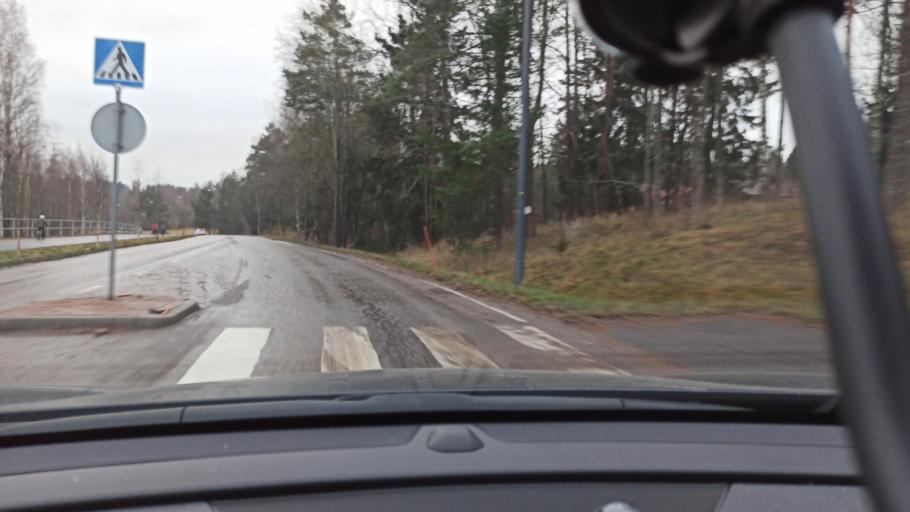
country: FI
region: Uusimaa
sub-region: Helsinki
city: Kirkkonummi
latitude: 60.1226
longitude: 24.4692
